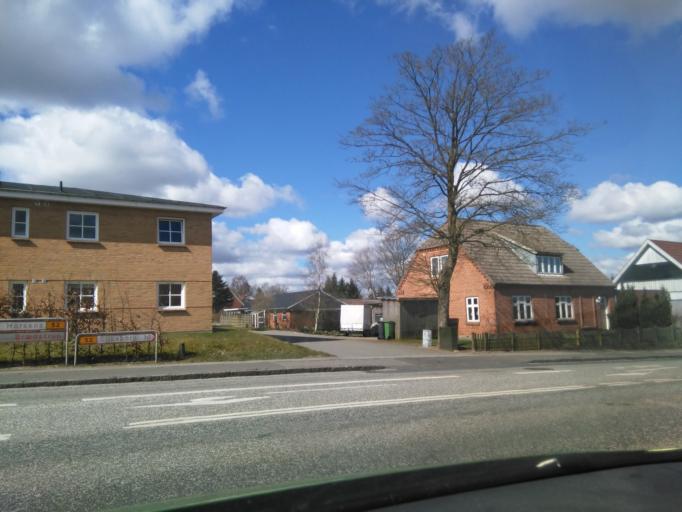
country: DK
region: Central Jutland
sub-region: Silkeborg Kommune
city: Virklund
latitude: 56.0844
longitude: 9.5708
